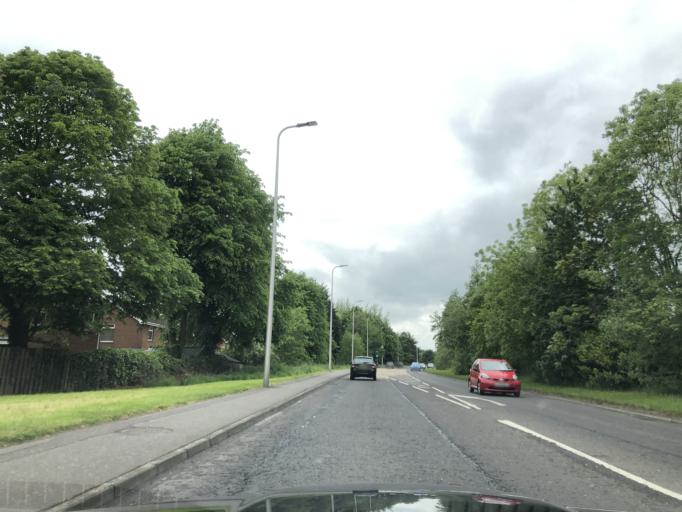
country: GB
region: Northern Ireland
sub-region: Lisburn District
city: Lisburn
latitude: 54.5165
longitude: -6.0652
